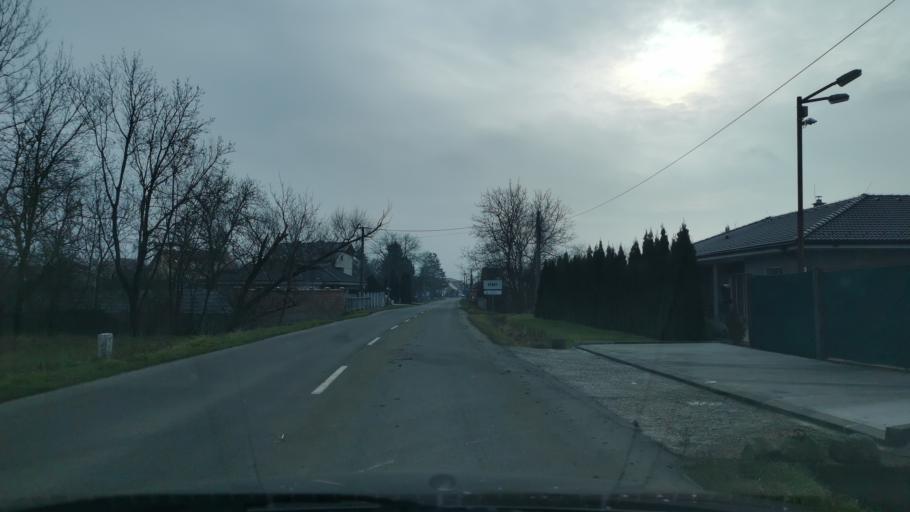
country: SK
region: Trnavsky
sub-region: Okres Senica
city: Senica
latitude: 48.7105
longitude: 17.3357
